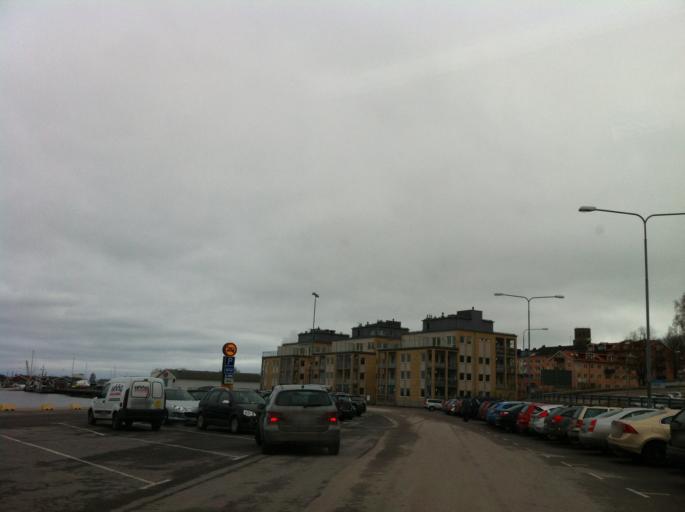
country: SE
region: Kalmar
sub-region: Vasterviks Kommun
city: Vaestervik
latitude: 57.7974
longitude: 16.6178
